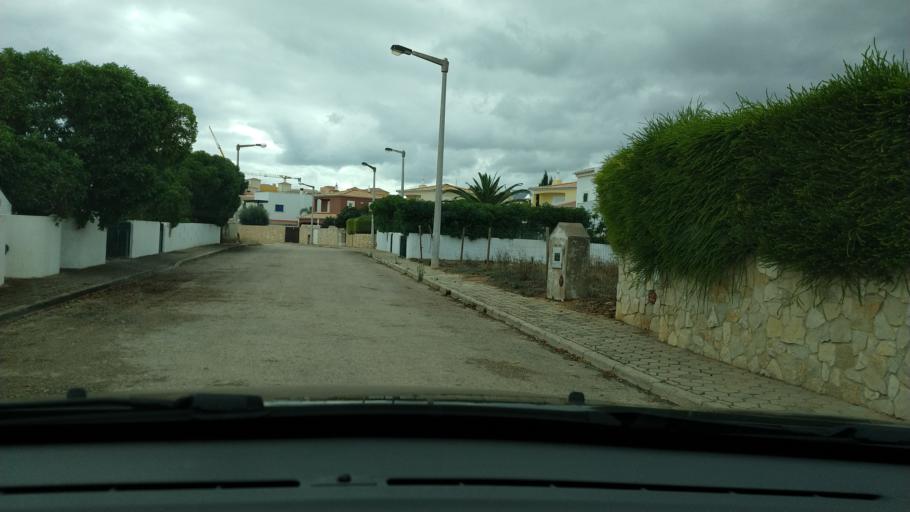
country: PT
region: Faro
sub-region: Lagos
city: Lagos
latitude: 37.0868
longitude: -8.6738
